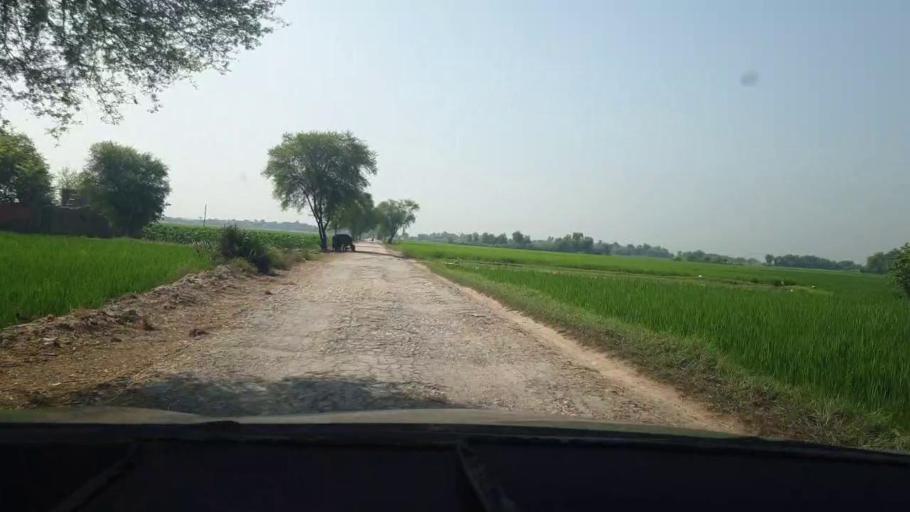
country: PK
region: Sindh
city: Kambar
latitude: 27.5662
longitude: 68.0570
